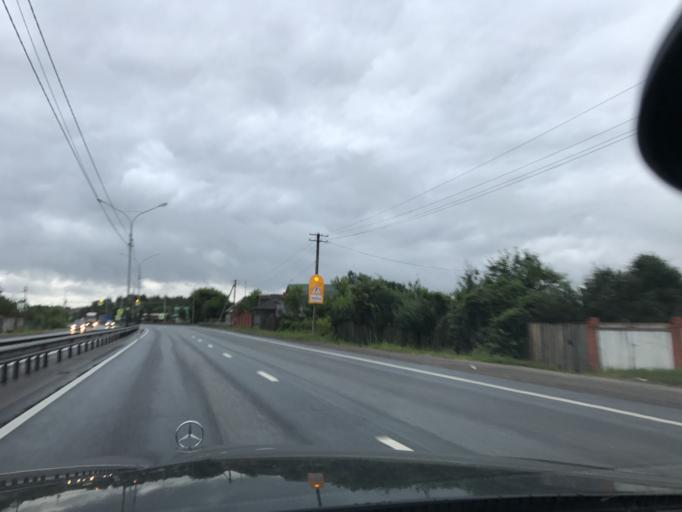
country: RU
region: Moskovskaya
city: Pavlovskiy Posad
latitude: 55.8495
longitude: 38.6655
